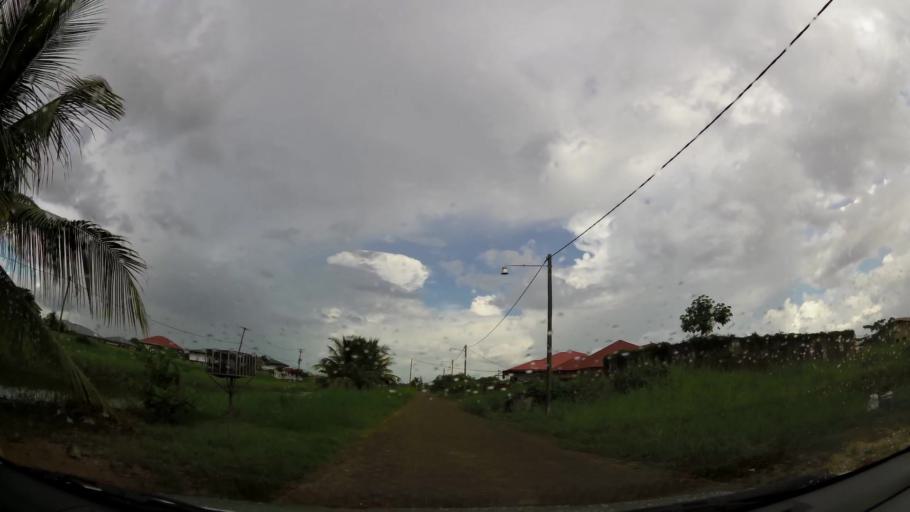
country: SR
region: Commewijne
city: Nieuw Amsterdam
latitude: 5.8634
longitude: -55.1158
